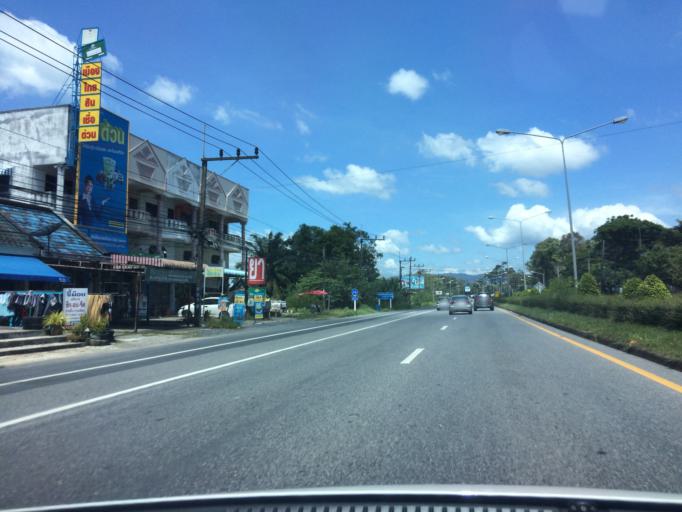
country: TH
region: Phangnga
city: Thai Mueang
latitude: 8.2222
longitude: 98.2986
